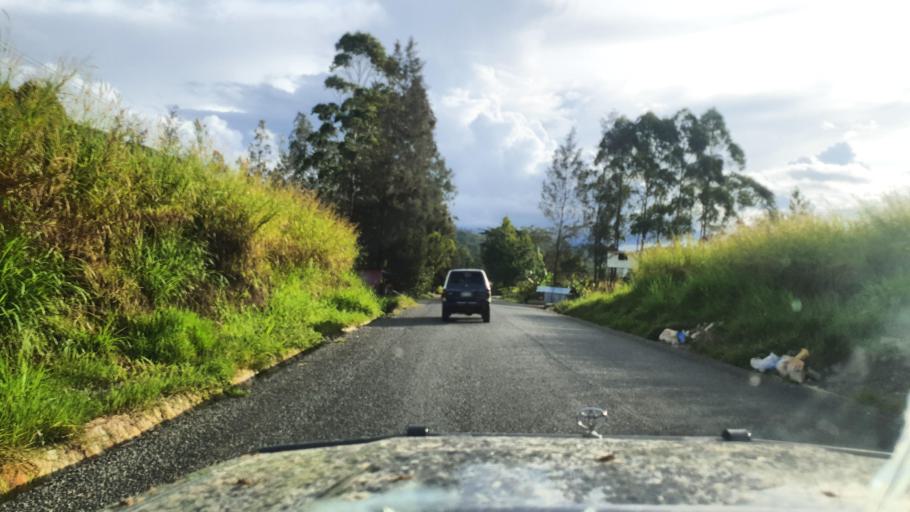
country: PG
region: Jiwaka
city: Minj
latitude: -5.8433
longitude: 144.5309
